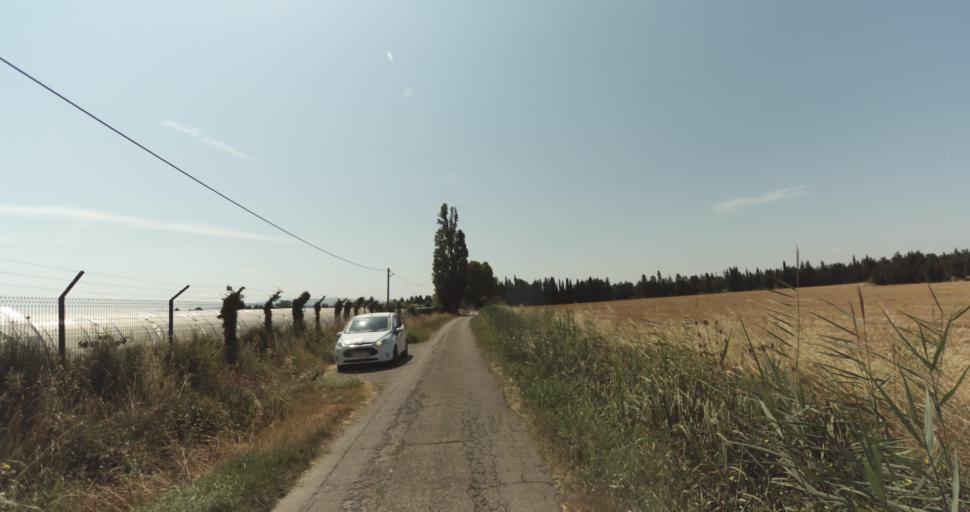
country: FR
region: Provence-Alpes-Cote d'Azur
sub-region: Departement du Vaucluse
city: Monteux
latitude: 44.0193
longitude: 5.0129
